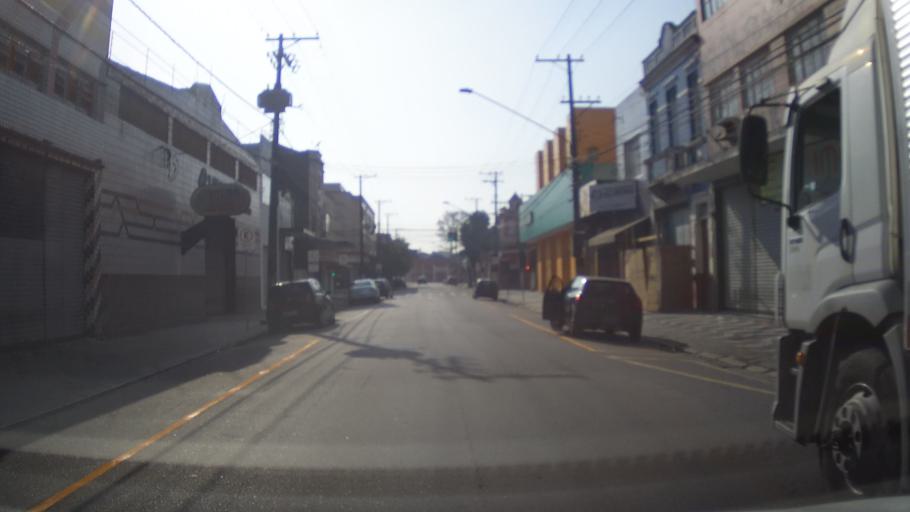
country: BR
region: Sao Paulo
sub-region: Santos
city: Santos
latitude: -23.9454
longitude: -46.3273
